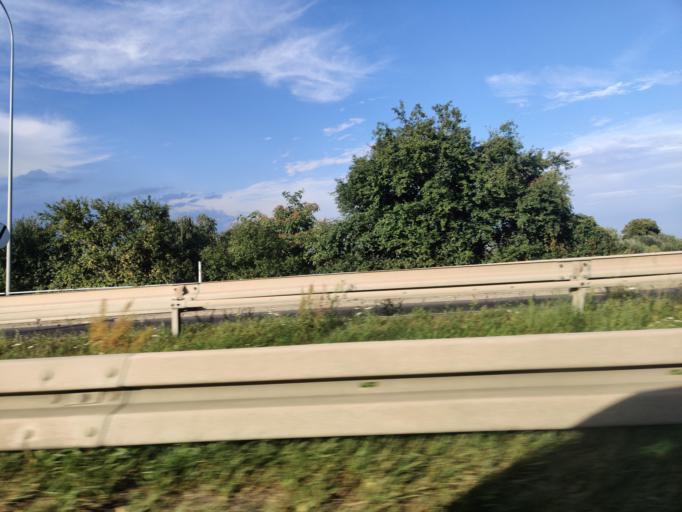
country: PL
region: Greater Poland Voivodeship
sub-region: Konin
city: Konin
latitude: 52.2150
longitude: 18.2563
